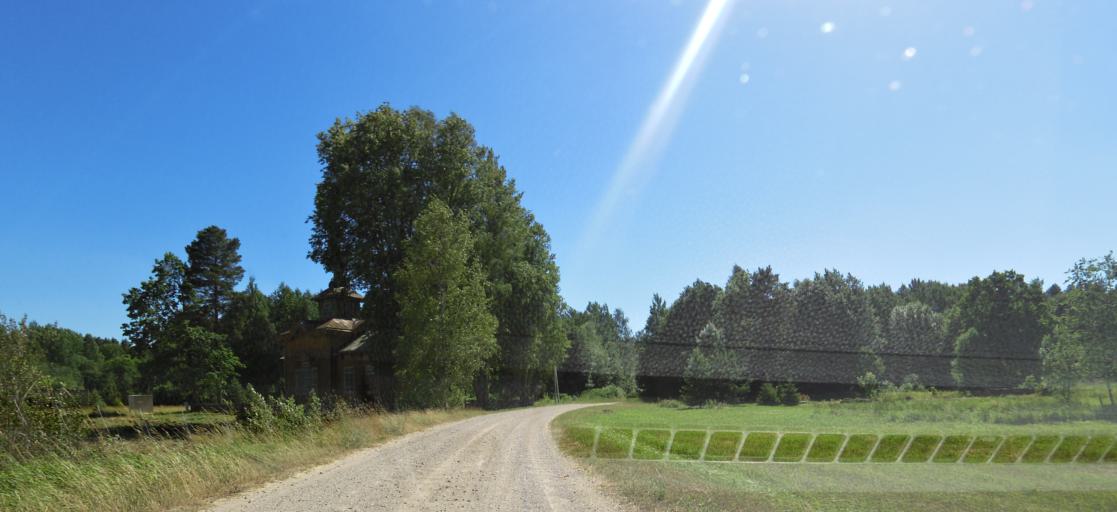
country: LT
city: Vabalninkas
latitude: 55.9274
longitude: 24.6516
